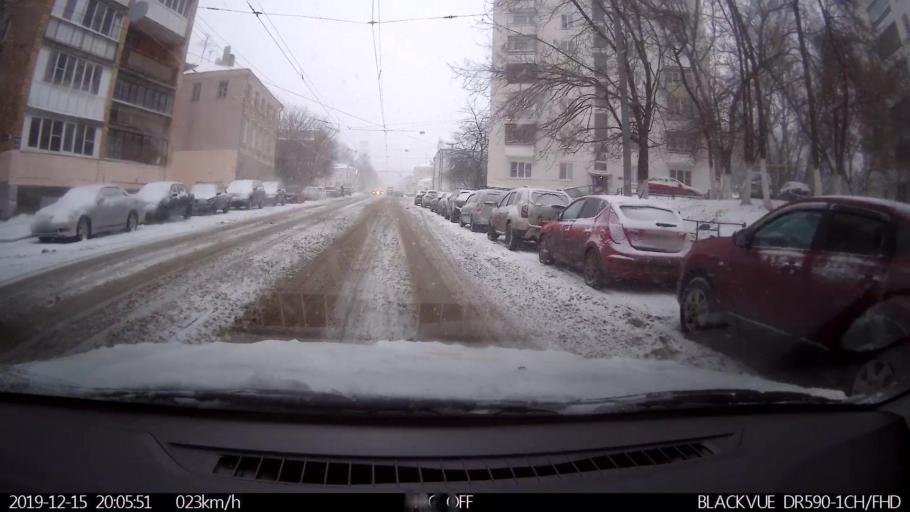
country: RU
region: Nizjnij Novgorod
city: Nizhniy Novgorod
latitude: 56.3246
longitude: 43.9917
